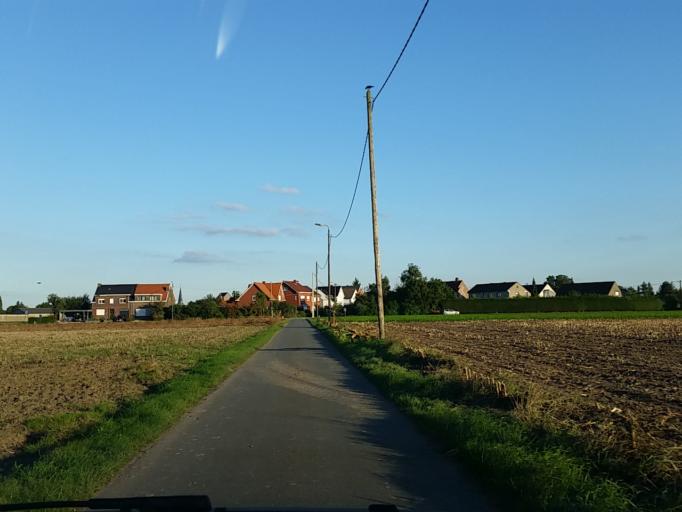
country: BE
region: Flanders
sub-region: Provincie Vlaams-Brabant
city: Steenokkerzeel
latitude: 50.9366
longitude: 4.4847
